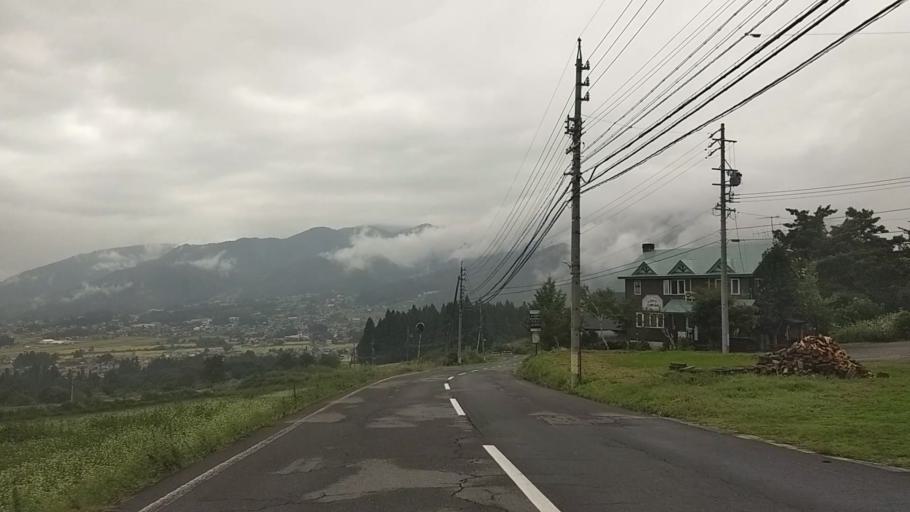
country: JP
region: Nagano
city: Iiyama
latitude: 36.8276
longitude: 138.4001
